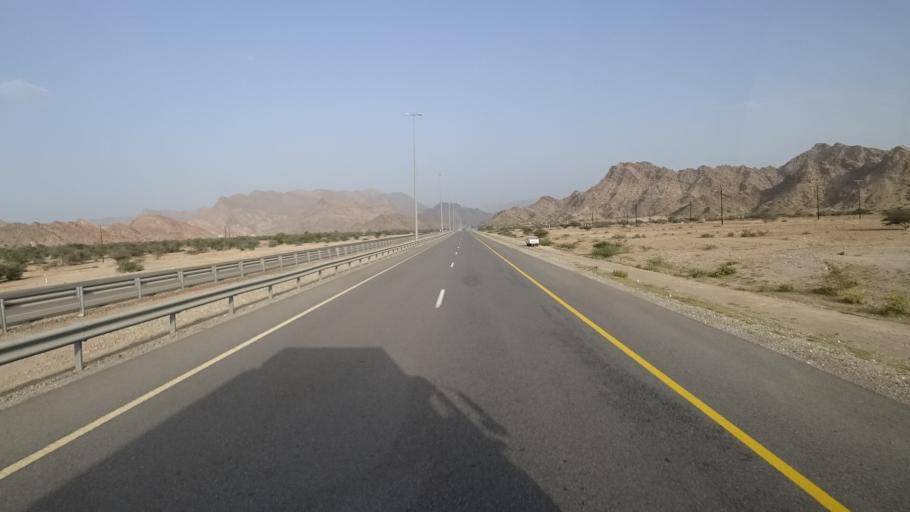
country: OM
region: Muhafazat Masqat
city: Muscat
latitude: 23.3678
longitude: 58.6464
